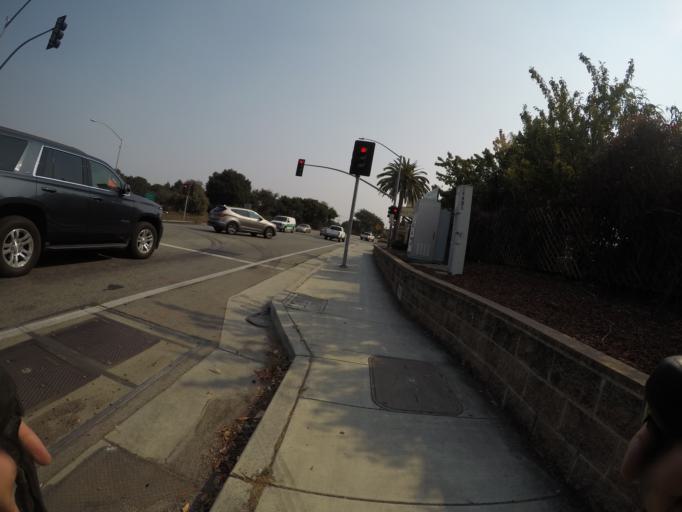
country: US
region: California
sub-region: Santa Cruz County
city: Live Oak
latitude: 36.9862
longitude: -121.9861
